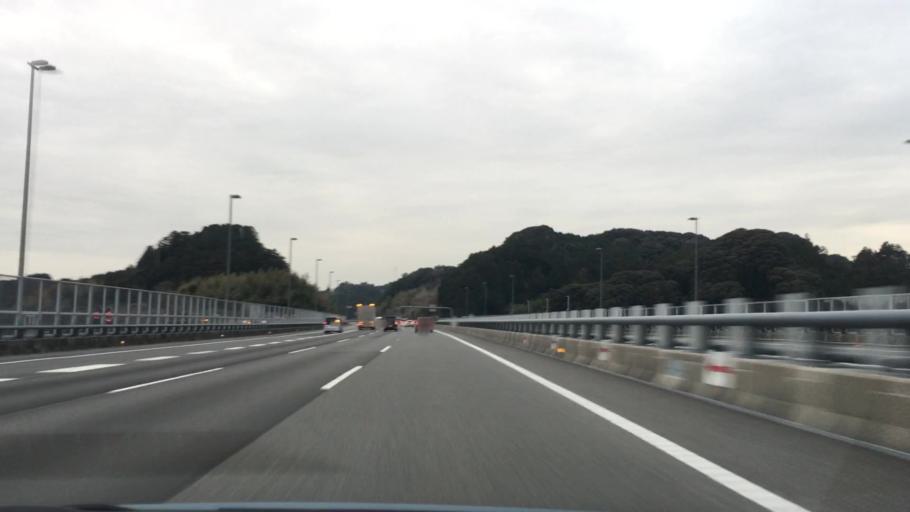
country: JP
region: Shizuoka
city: Mori
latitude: 34.8273
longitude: 137.8990
